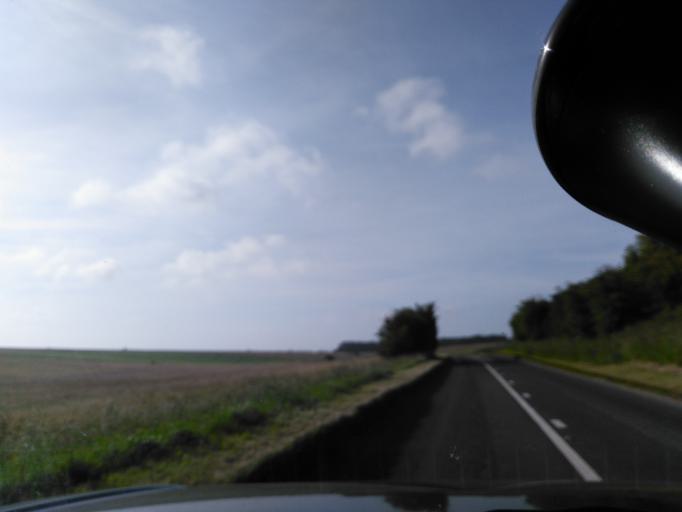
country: GB
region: England
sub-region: Wiltshire
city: Market Lavington
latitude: 51.2370
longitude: -1.9723
